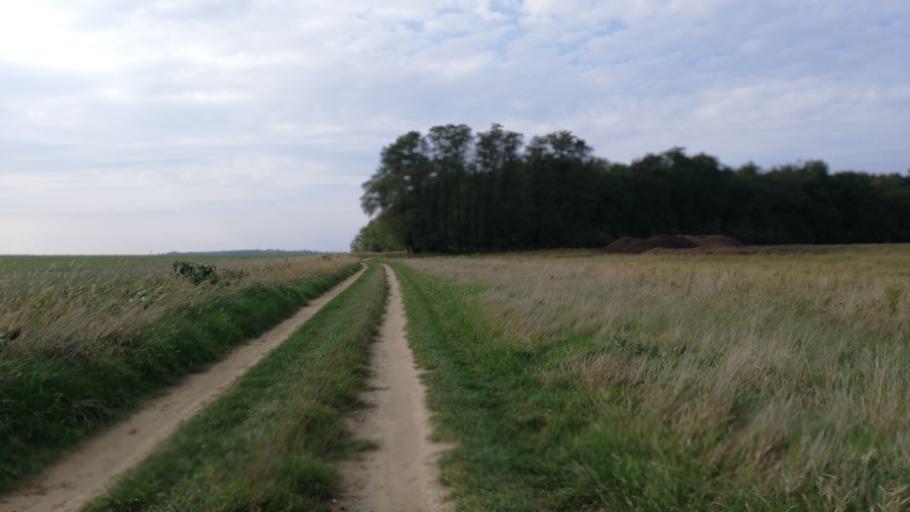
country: CZ
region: South Moravian
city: Sudomerice
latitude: 48.8191
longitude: 17.2745
